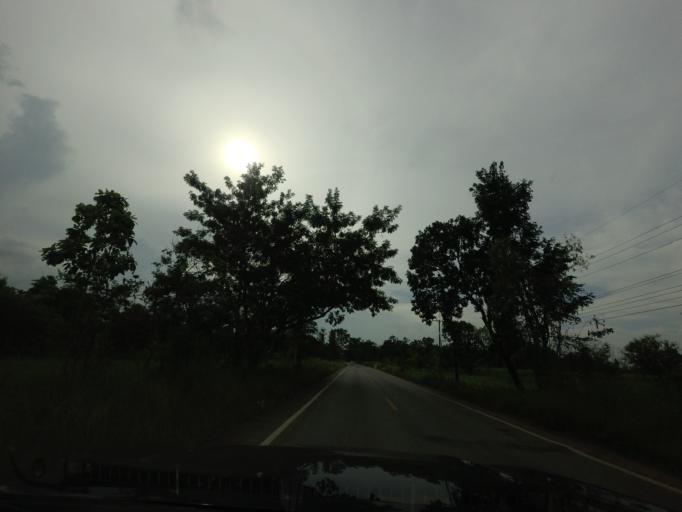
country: TH
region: Changwat Nong Bua Lamphu
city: Nong Bua Lamphu
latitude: 17.3675
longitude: 102.3651
